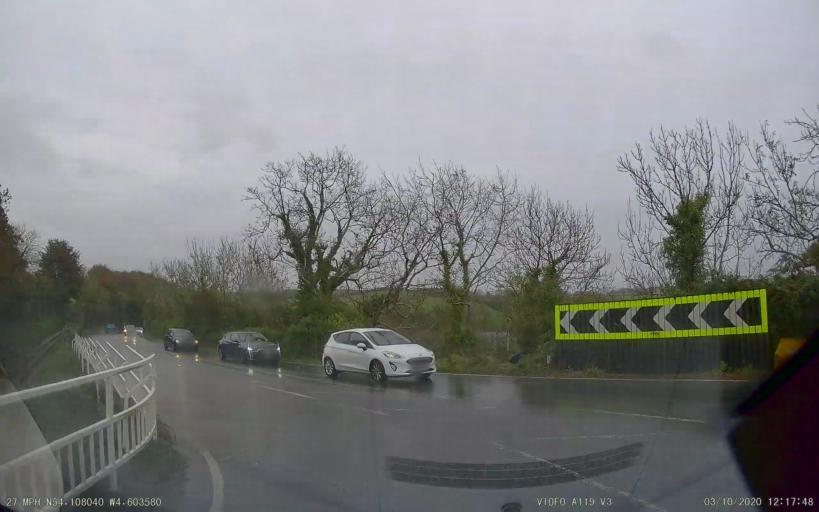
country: IM
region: Castletown
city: Castletown
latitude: 54.1080
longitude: -4.6036
